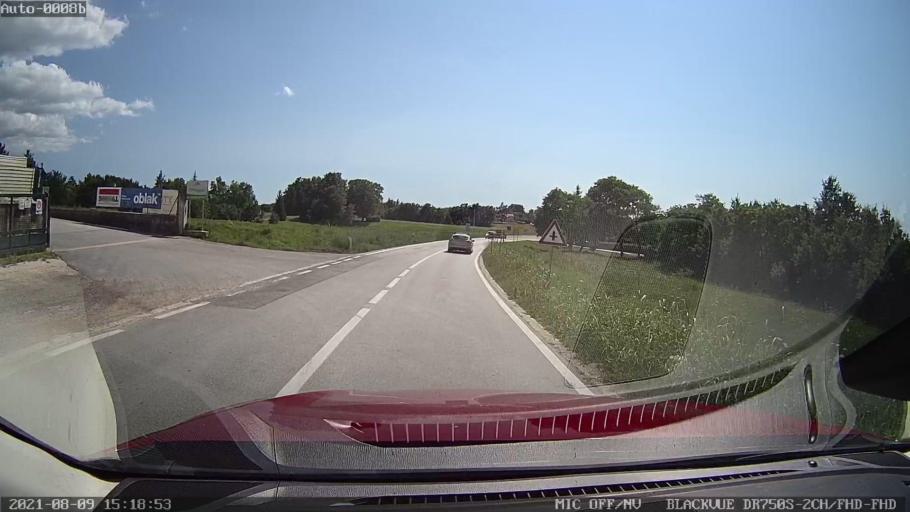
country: HR
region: Istarska
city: Pazin
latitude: 45.2185
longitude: 13.9043
